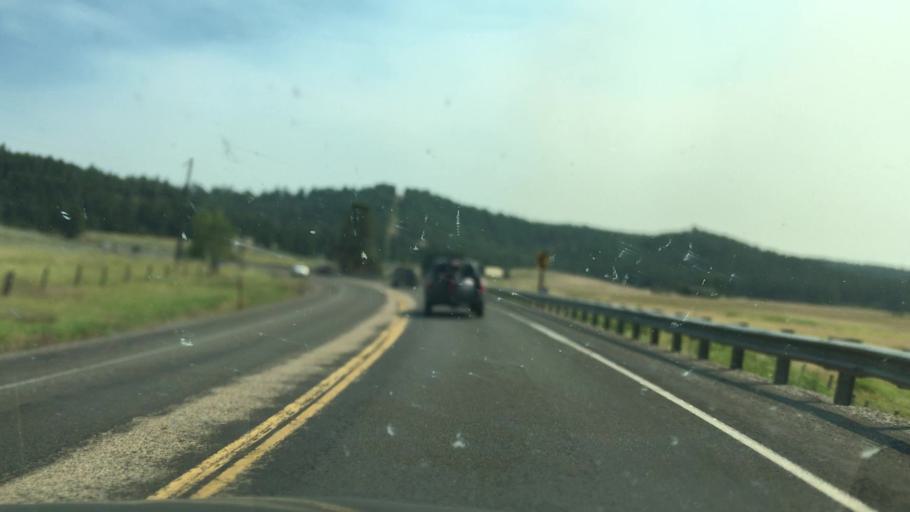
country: US
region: Idaho
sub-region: Valley County
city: Cascade
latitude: 44.5985
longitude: -116.0479
